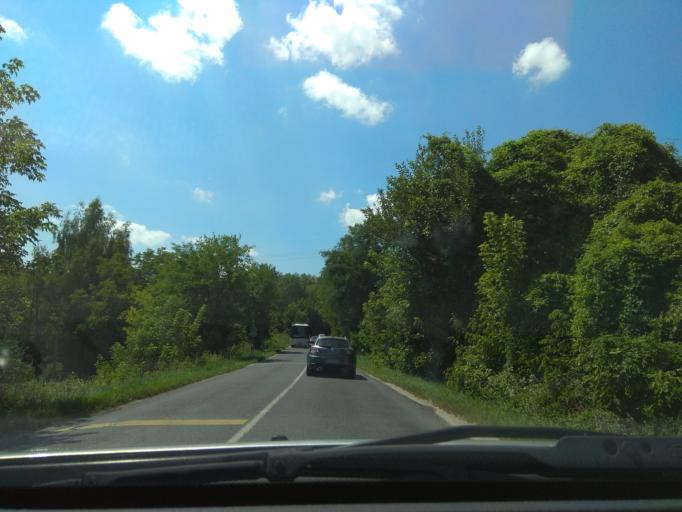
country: HU
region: Borsod-Abauj-Zemplen
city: Harsany
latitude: 48.0258
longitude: 20.7666
